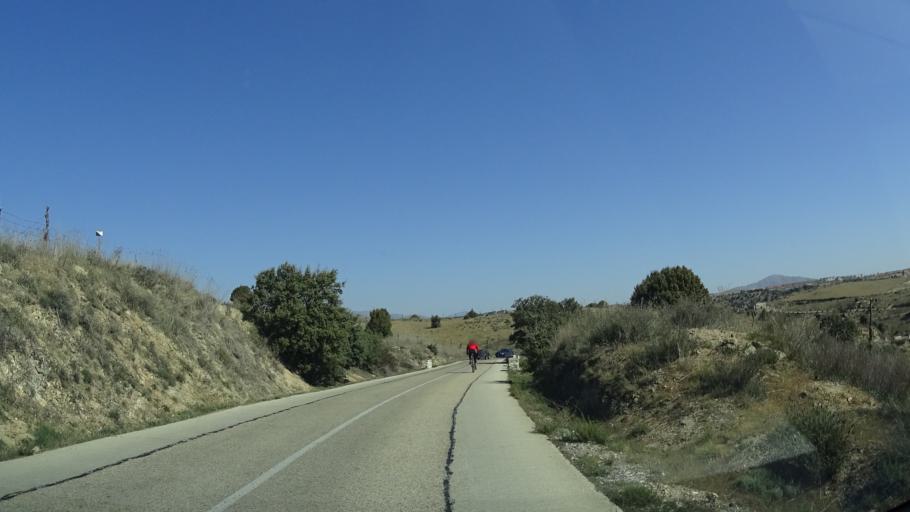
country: ES
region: Madrid
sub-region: Provincia de Madrid
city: Colmenar Viejo
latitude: 40.6448
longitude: -3.8110
